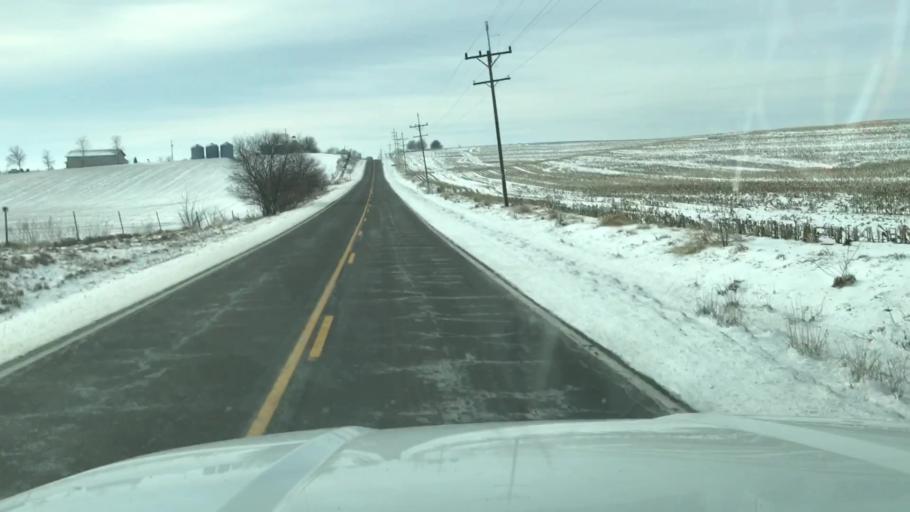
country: US
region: Missouri
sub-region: Holt County
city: Oregon
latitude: 40.0685
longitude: -95.1355
